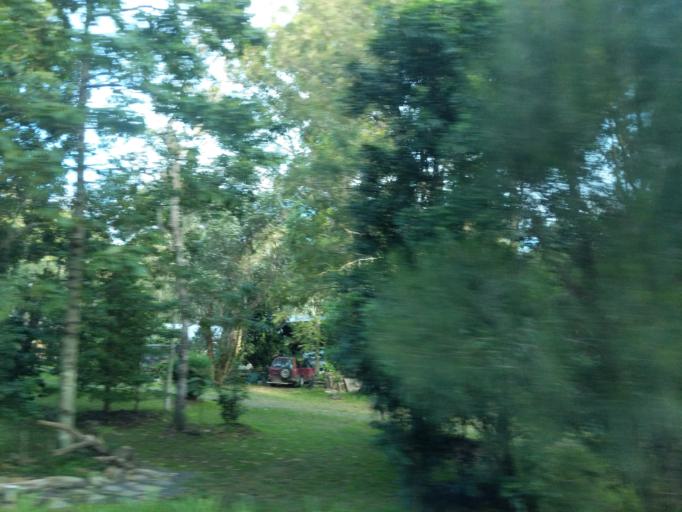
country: AU
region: New South Wales
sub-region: Port Stephens Shire
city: Port Stephens
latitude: -32.6657
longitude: 152.0168
